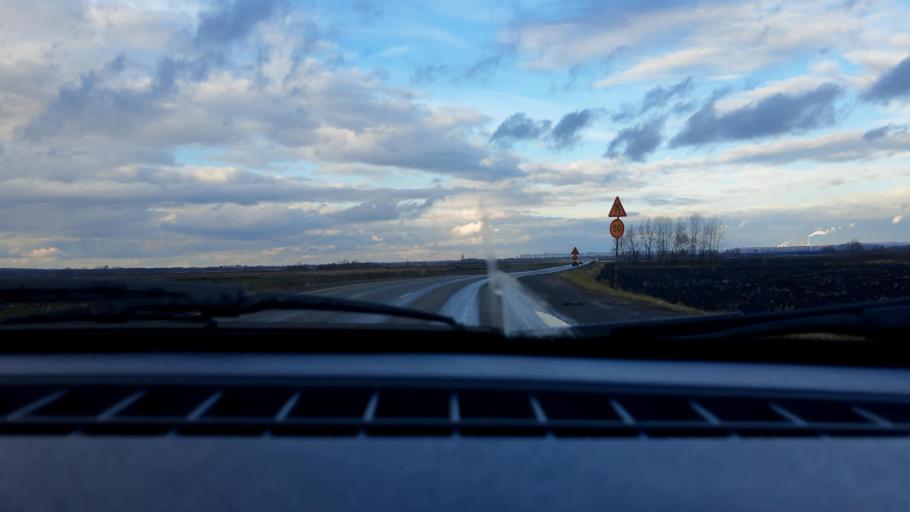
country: RU
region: Bashkortostan
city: Ufa
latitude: 54.8036
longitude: 55.9637
